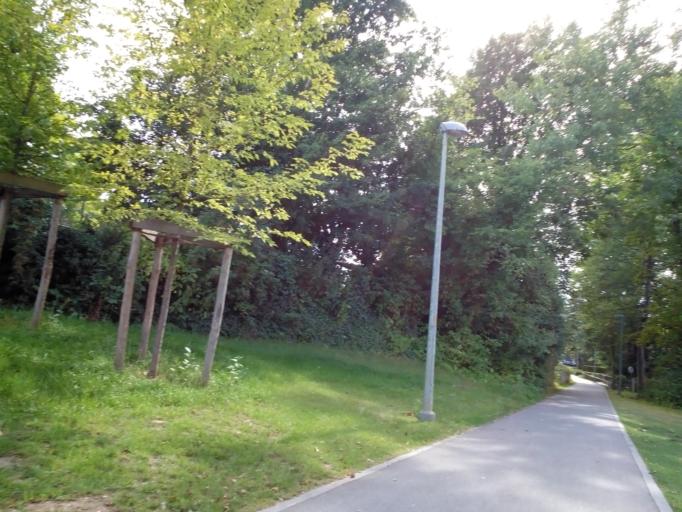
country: BE
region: Flanders
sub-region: Provincie Vlaams-Brabant
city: Leuven
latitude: 50.8923
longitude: 4.7258
